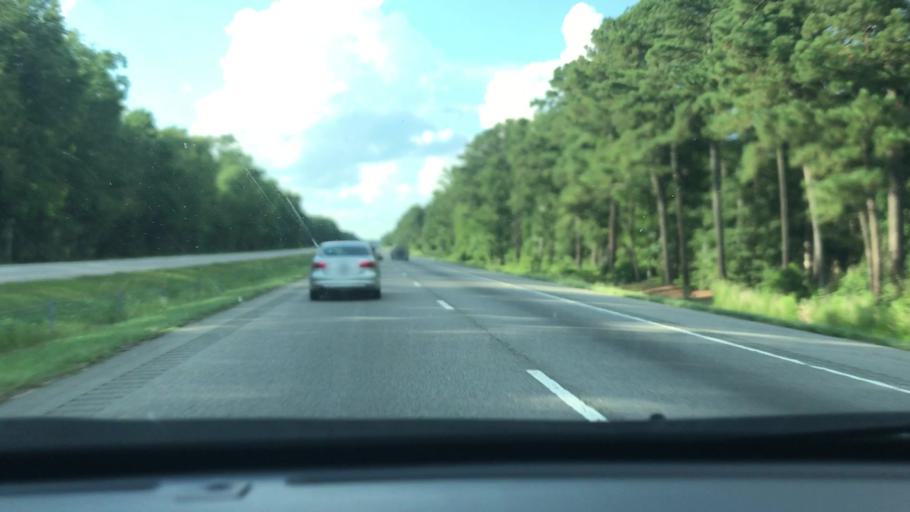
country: US
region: North Carolina
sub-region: Robeson County
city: Saint Pauls
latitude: 34.7368
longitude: -78.9972
